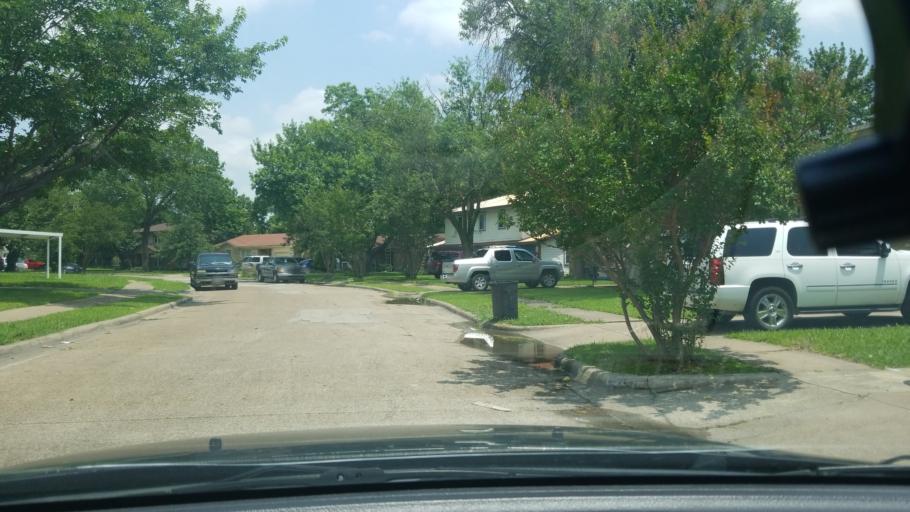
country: US
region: Texas
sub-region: Dallas County
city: Mesquite
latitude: 32.7940
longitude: -96.6410
